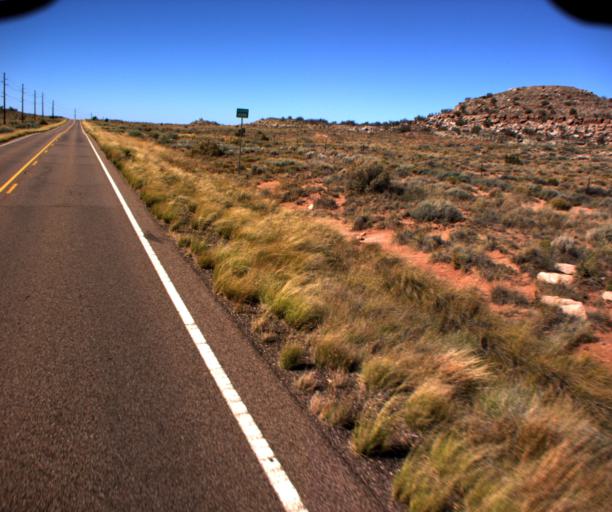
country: US
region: Arizona
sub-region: Navajo County
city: Taylor
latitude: 34.4972
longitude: -110.2031
